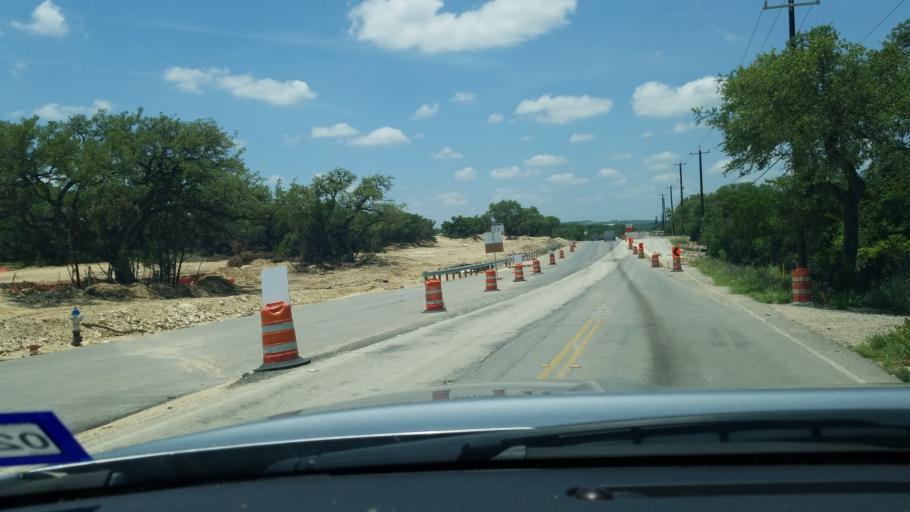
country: US
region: Texas
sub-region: Bexar County
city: Timberwood Park
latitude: 29.7083
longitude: -98.5008
